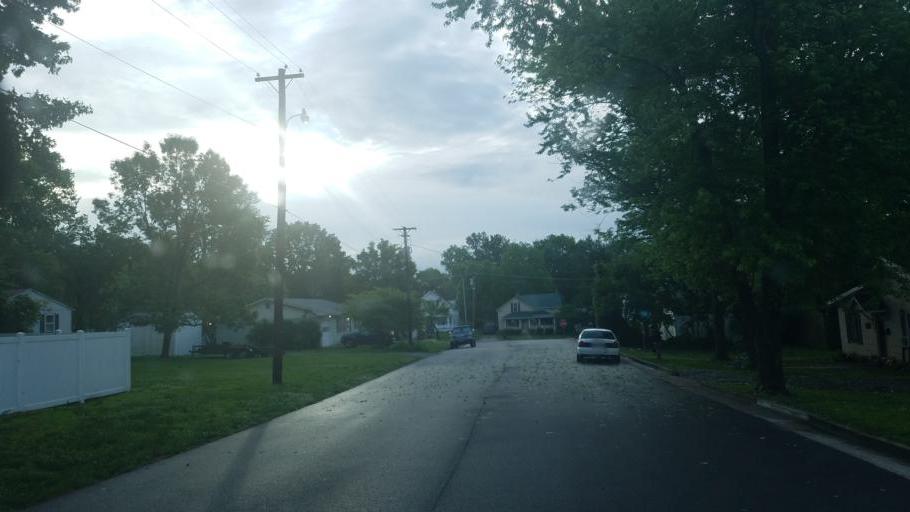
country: US
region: Missouri
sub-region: Moniteau County
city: California
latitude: 38.6248
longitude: -92.5680
